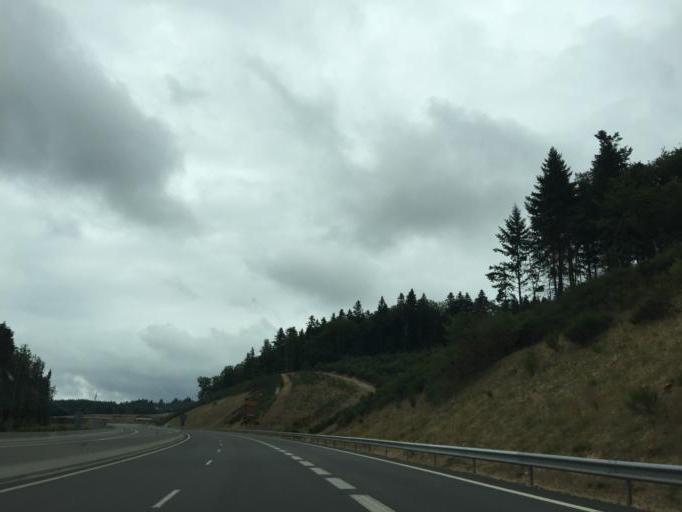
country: FR
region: Rhone-Alpes
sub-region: Departement de la Loire
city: Bussieres
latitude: 45.8692
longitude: 4.2812
